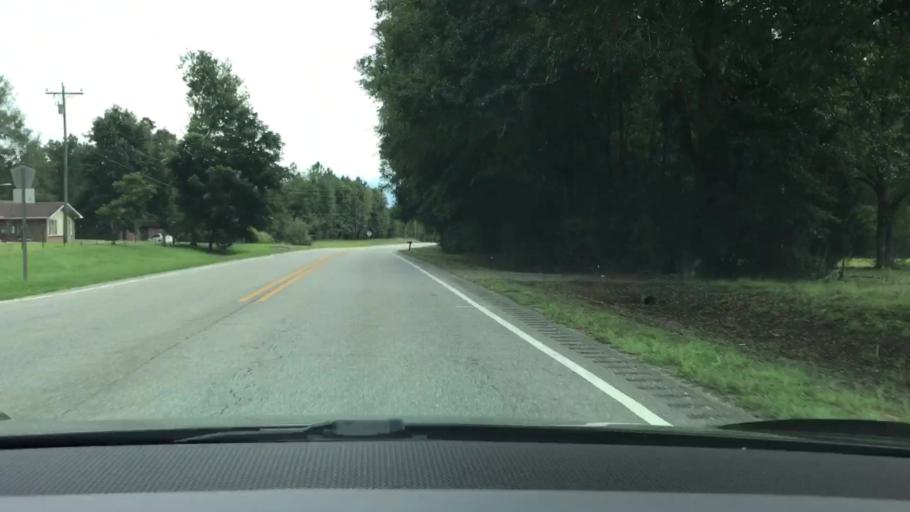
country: US
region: Alabama
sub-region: Pike County
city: Troy
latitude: 31.6363
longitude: -85.9723
